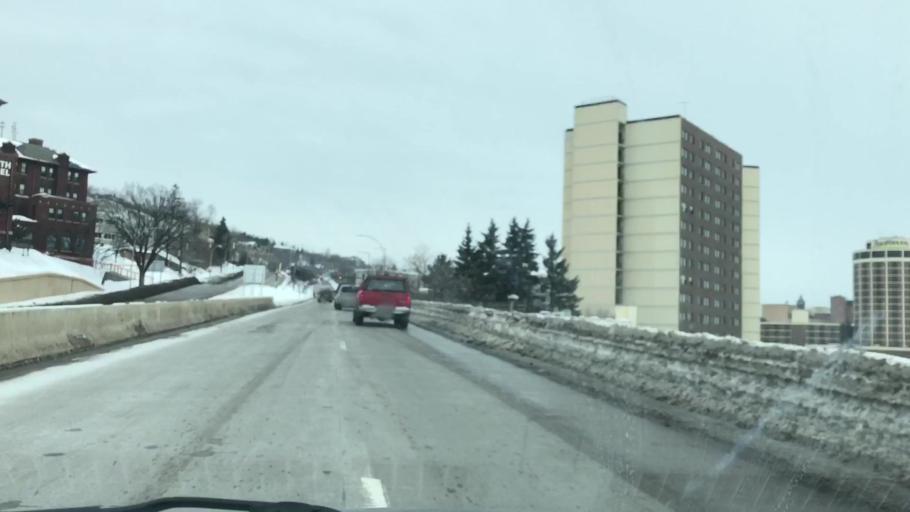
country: US
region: Minnesota
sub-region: Saint Louis County
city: Duluth
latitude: 46.7793
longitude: -92.1079
